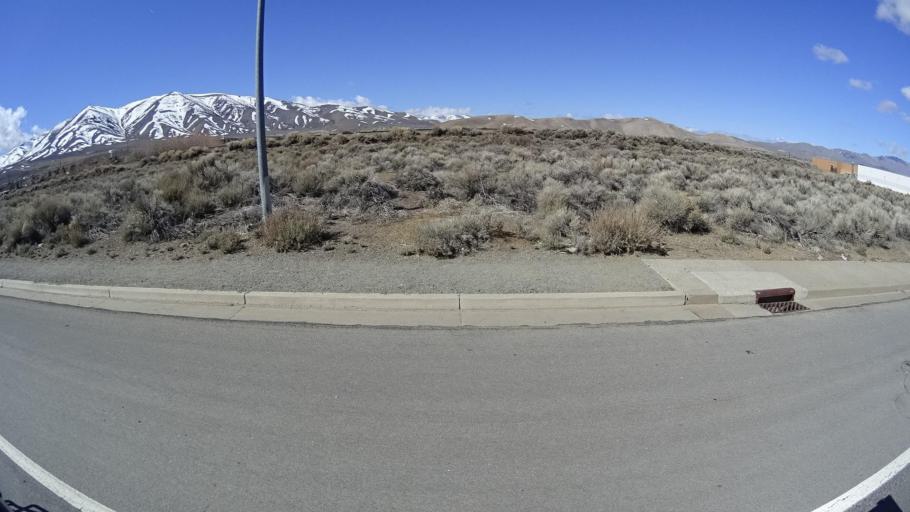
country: US
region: Nevada
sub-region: Washoe County
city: Lemmon Valley
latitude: 39.6302
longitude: -119.8823
